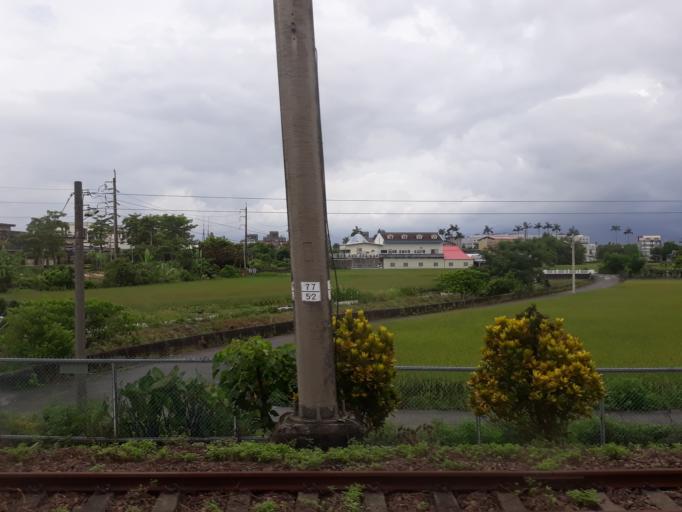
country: TW
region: Taiwan
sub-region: Yilan
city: Yilan
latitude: 24.6986
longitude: 121.7753
